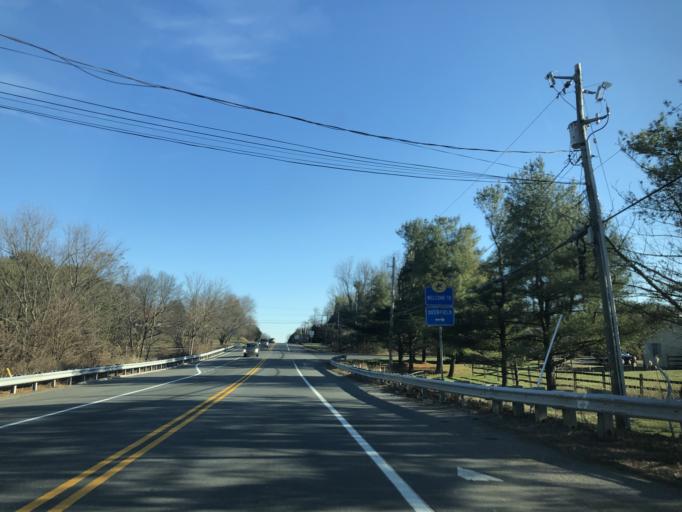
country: US
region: Delaware
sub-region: New Castle County
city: Hockessin
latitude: 39.7945
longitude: -75.7140
